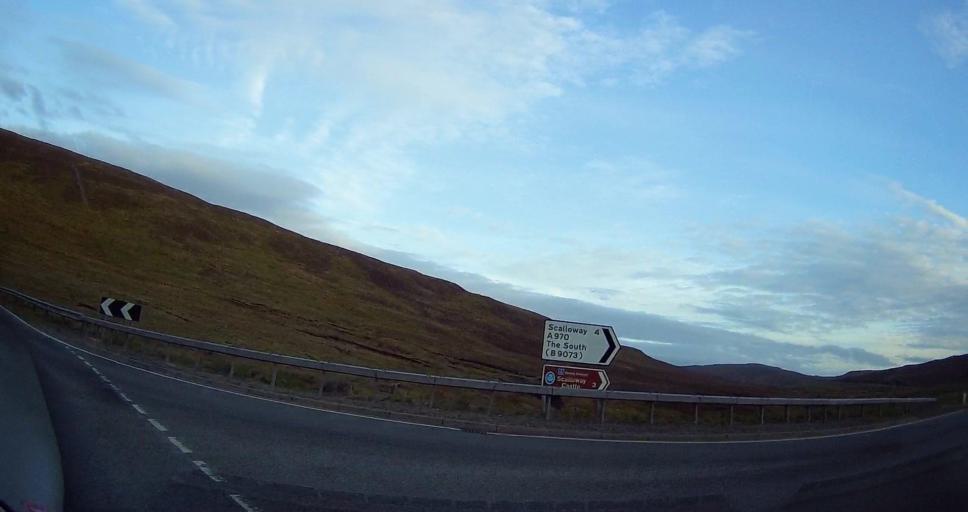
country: GB
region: Scotland
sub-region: Shetland Islands
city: Lerwick
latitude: 60.1608
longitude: -1.2264
